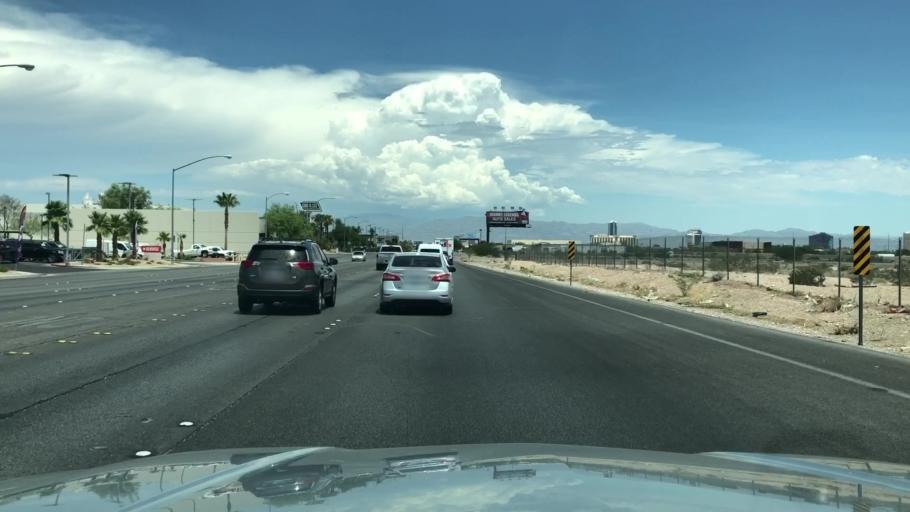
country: US
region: Nevada
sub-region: Clark County
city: Spring Valley
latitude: 36.0774
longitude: -115.2078
